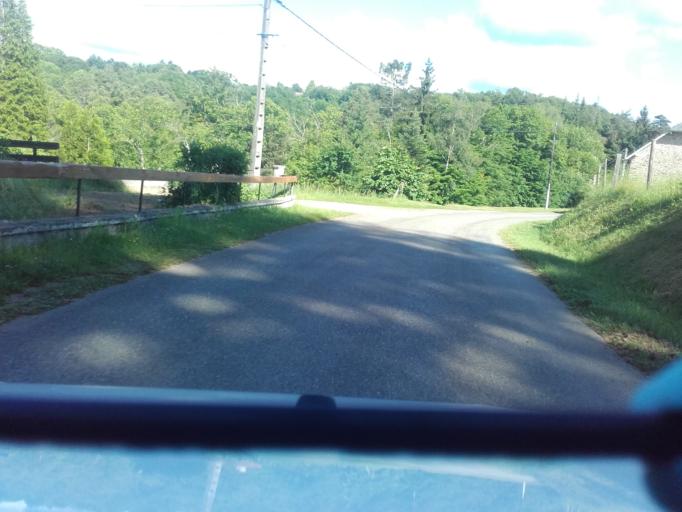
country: FR
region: Limousin
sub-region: Departement de la Correze
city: Laguenne
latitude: 45.2120
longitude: 1.8613
